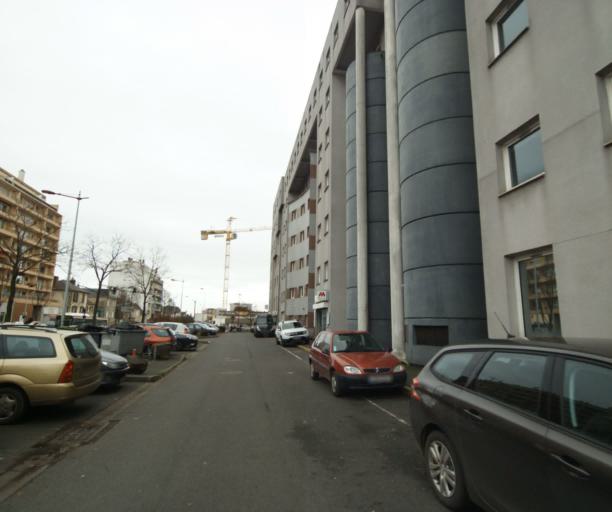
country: FR
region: Pays de la Loire
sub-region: Departement de la Sarthe
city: Le Mans
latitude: 47.9973
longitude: 0.2162
